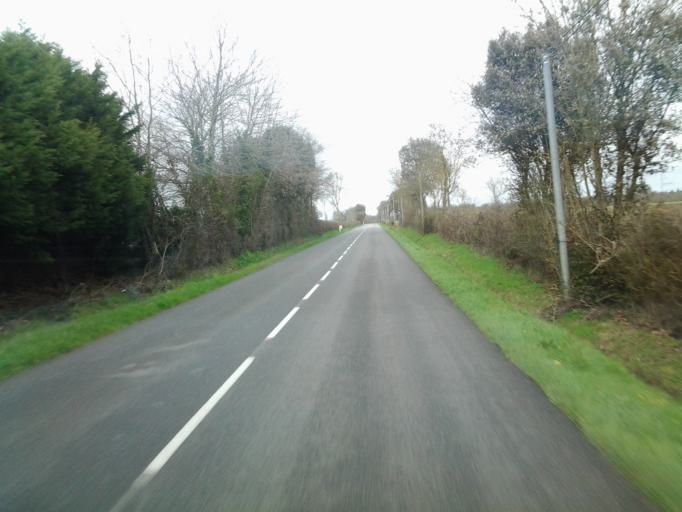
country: FR
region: Pays de la Loire
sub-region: Departement de la Vendee
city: Avrille
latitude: 46.4764
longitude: -1.4830
